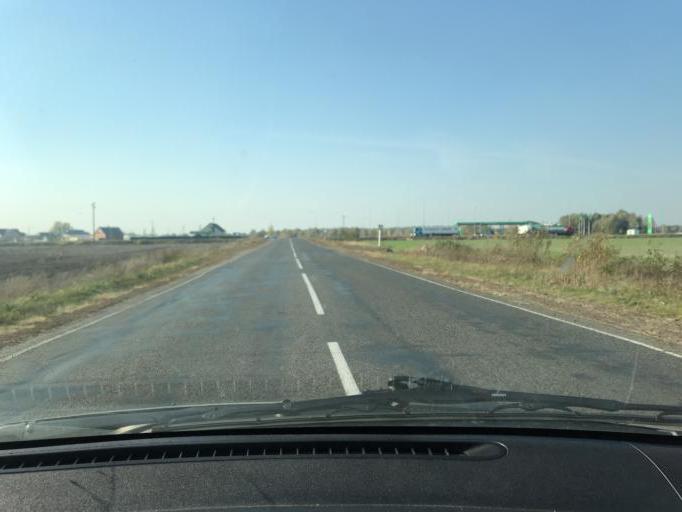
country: BY
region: Brest
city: Davyd-Haradok
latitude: 52.0695
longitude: 27.2442
